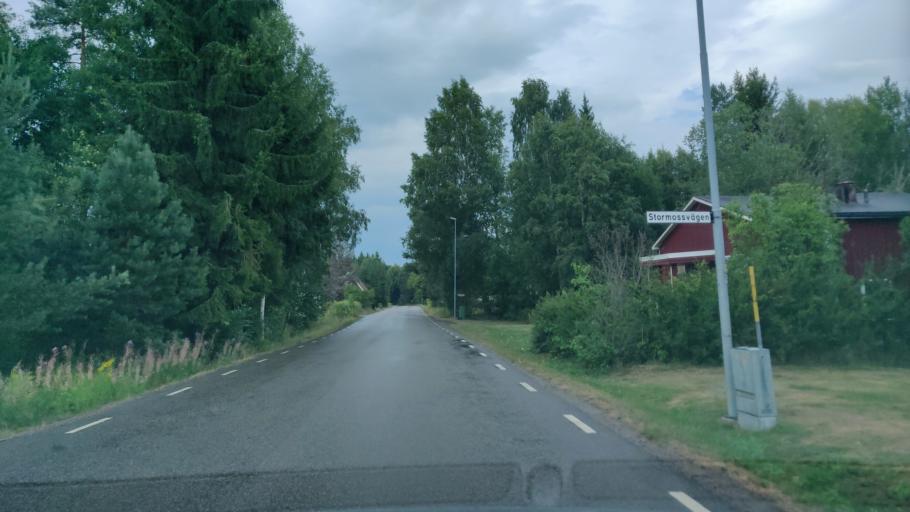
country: SE
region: Vaermland
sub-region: Munkfors Kommun
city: Munkfors
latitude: 59.8562
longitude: 13.5533
